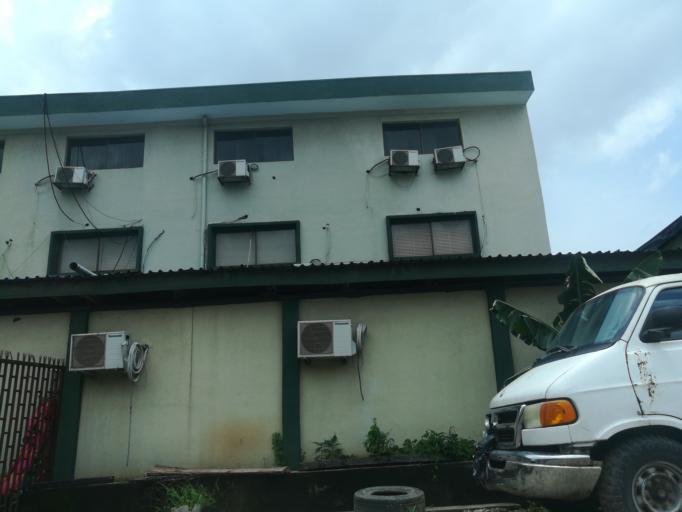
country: NG
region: Lagos
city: Somolu
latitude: 6.5535
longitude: 3.3656
